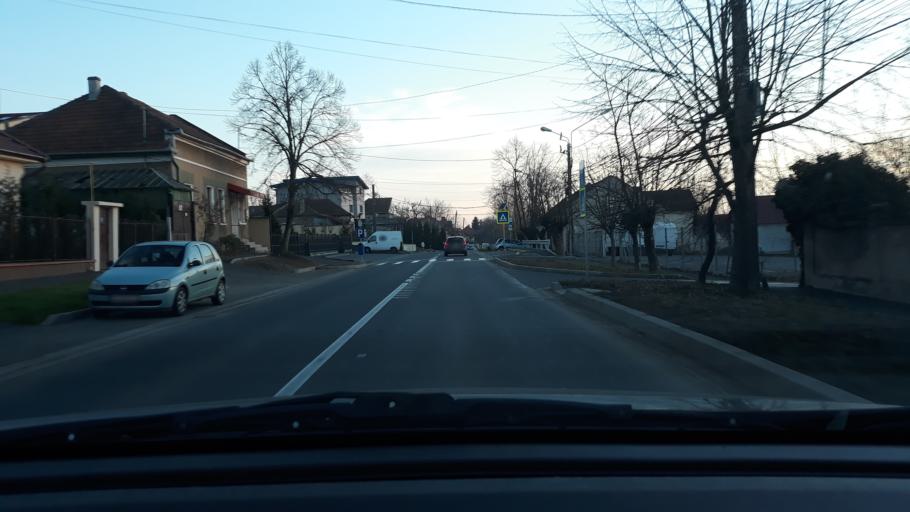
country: RO
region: Bihor
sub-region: Comuna Biharea
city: Oradea
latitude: 47.0860
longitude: 21.9269
